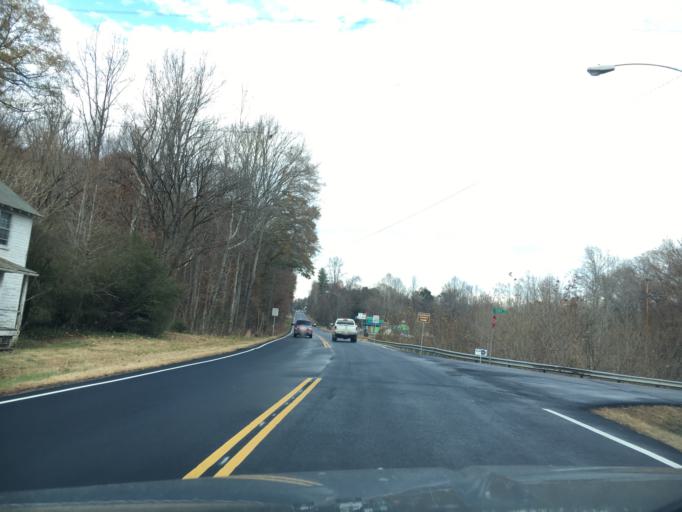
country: US
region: Virginia
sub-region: Prince Edward County
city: Farmville
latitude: 37.3109
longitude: -78.3869
